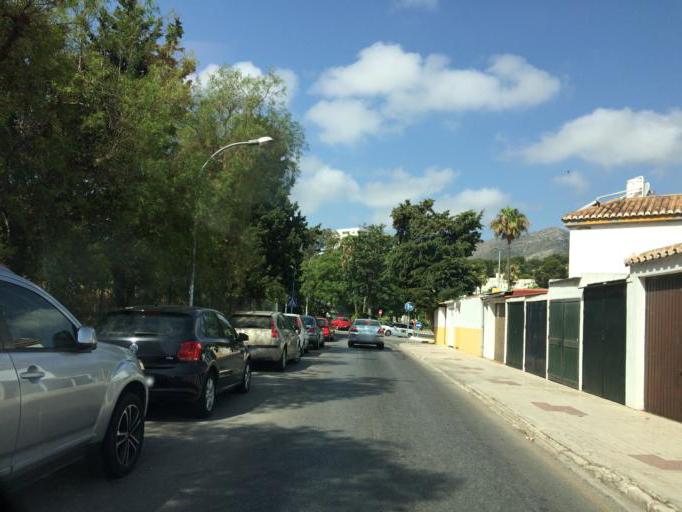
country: ES
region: Andalusia
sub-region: Provincia de Malaga
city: Torremolinos
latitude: 36.6397
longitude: -4.4953
